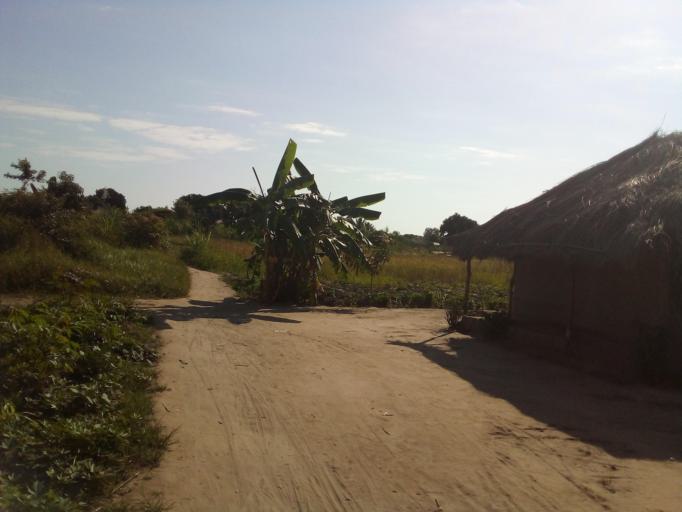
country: MZ
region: Zambezia
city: Quelimane
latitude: -17.5564
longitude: 36.6999
